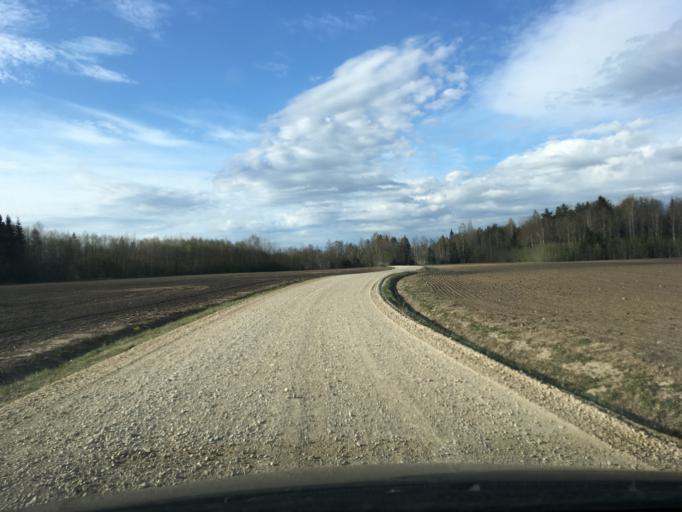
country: EE
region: Raplamaa
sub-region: Maerjamaa vald
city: Marjamaa
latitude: 58.9820
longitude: 24.3625
